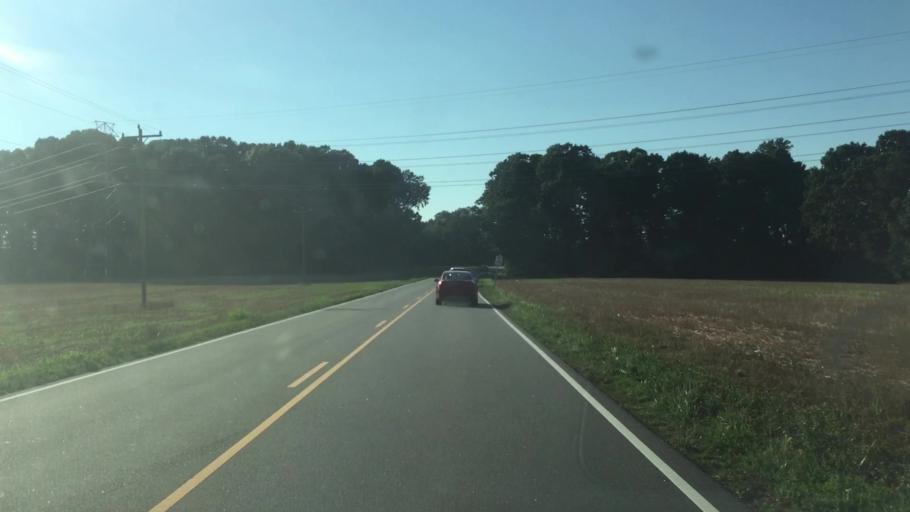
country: US
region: North Carolina
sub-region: Gaston County
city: Davidson
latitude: 35.4796
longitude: -80.7541
